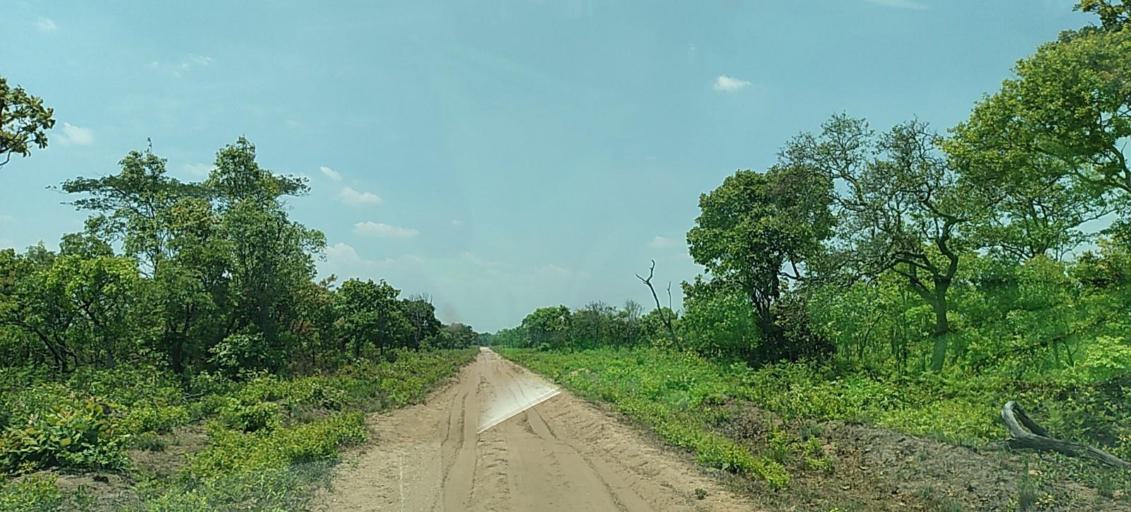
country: CD
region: Katanga
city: Kolwezi
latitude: -11.3380
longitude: 25.2220
